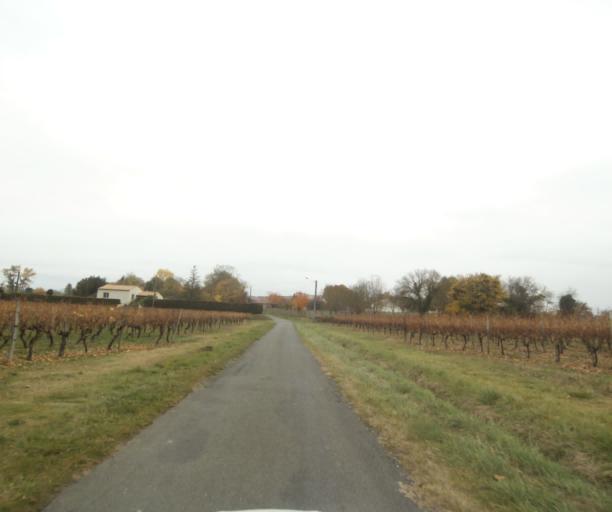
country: FR
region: Poitou-Charentes
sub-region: Departement de la Charente-Maritime
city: Chermignac
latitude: 45.7077
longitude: -0.6662
